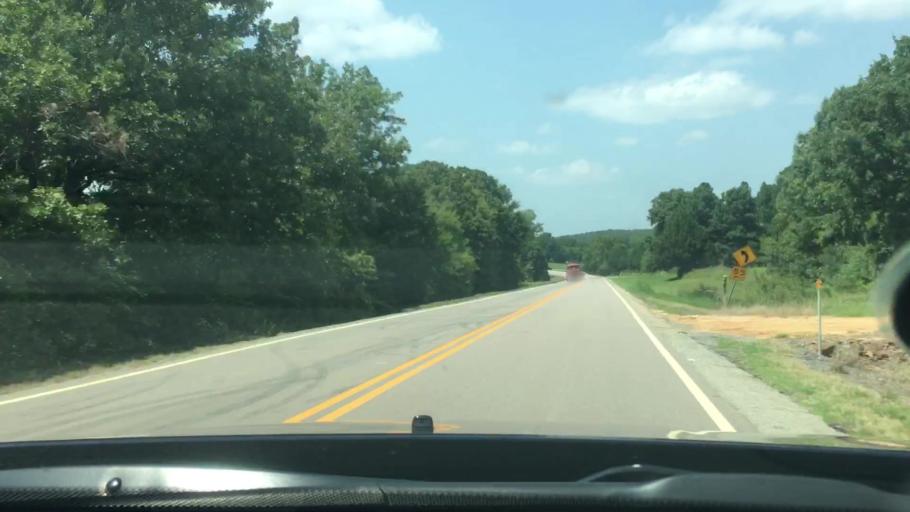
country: US
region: Oklahoma
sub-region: Coal County
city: Coalgate
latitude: 34.3714
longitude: -96.3864
